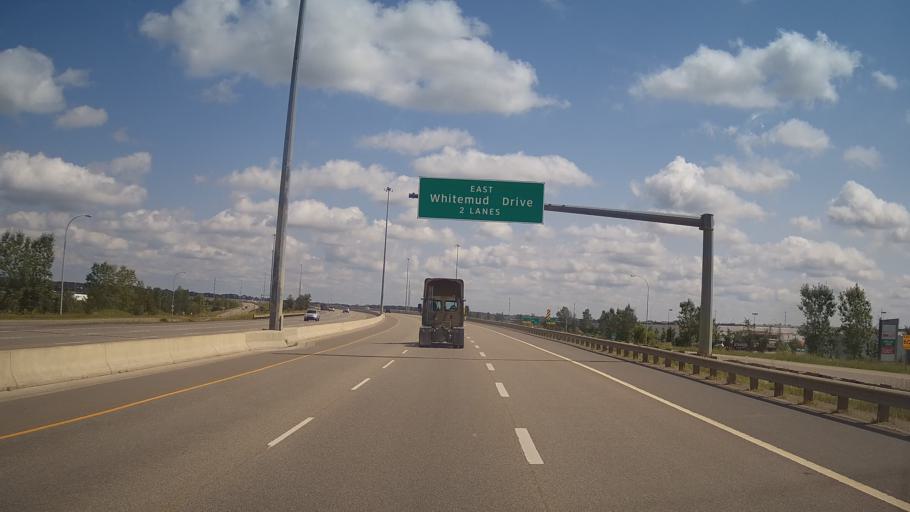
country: CA
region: Alberta
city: Sherwood Park
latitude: 53.4825
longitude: -113.3745
